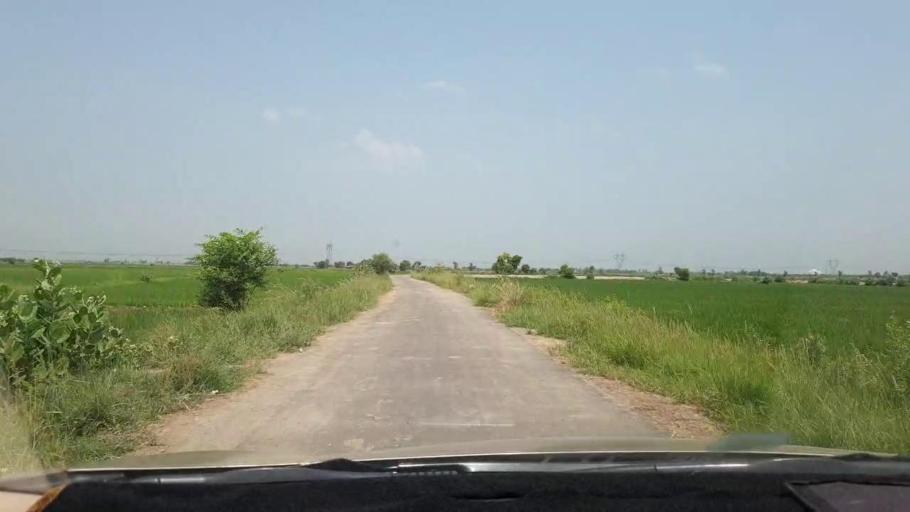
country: PK
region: Sindh
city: Naudero
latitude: 27.6663
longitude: 68.3241
